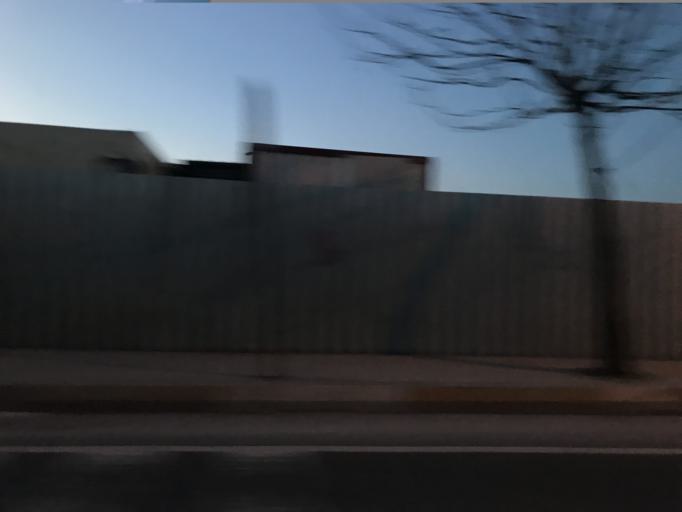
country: TR
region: Istanbul
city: Pendik
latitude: 40.9036
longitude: 29.2755
